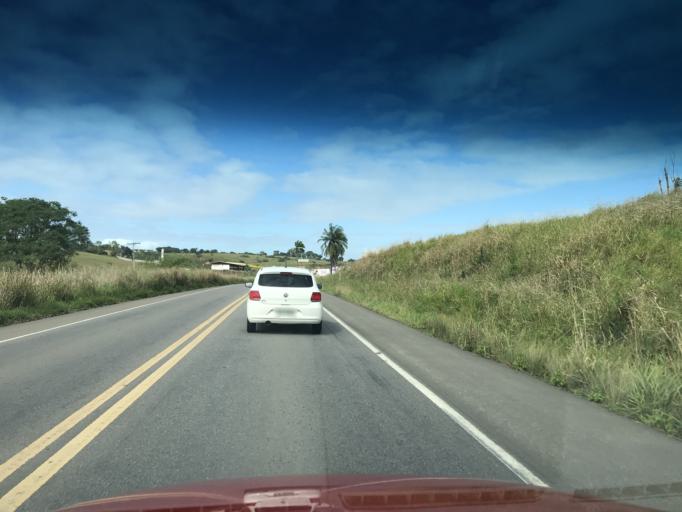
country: BR
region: Bahia
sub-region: Conceicao Do Almeida
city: Muritiba
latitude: -12.9430
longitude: -39.2516
